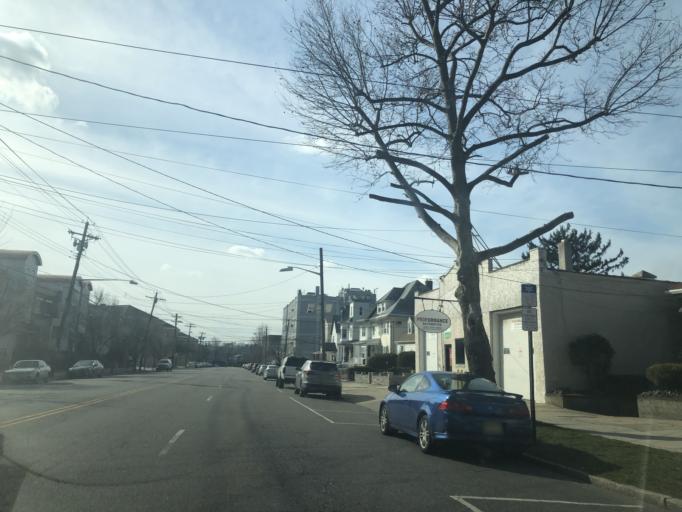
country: US
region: New Jersey
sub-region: Hudson County
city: Bayonne
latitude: 40.6483
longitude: -74.1305
